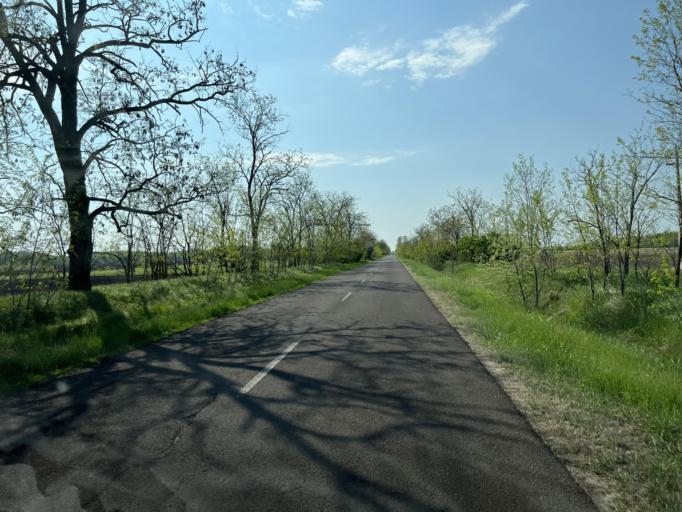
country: HU
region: Pest
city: Jaszkarajeno
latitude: 47.0262
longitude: 20.0368
